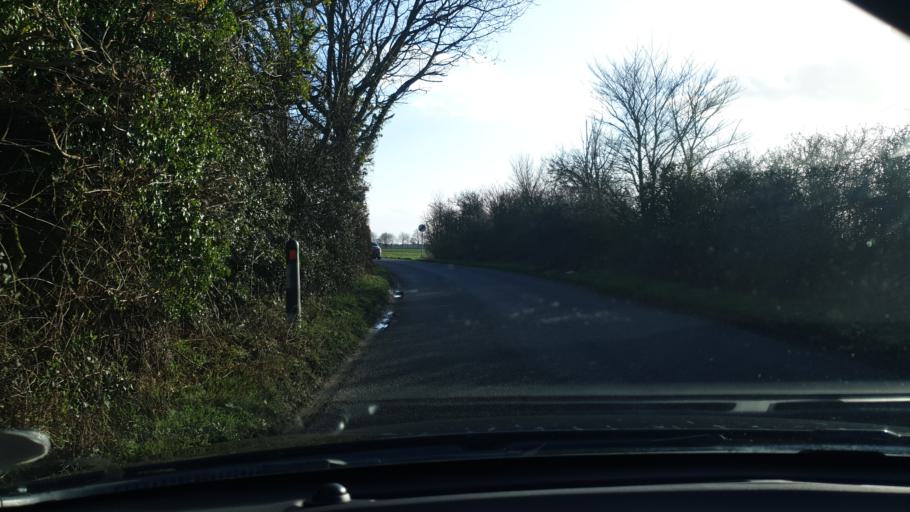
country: GB
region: England
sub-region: Essex
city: Little Clacton
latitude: 51.8940
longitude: 1.1471
